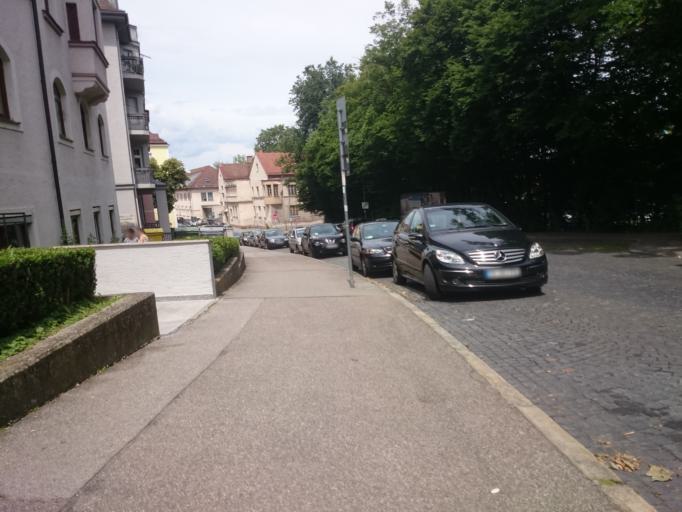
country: DE
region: Bavaria
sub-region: Swabia
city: Augsburg
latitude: 48.3793
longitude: 10.8914
